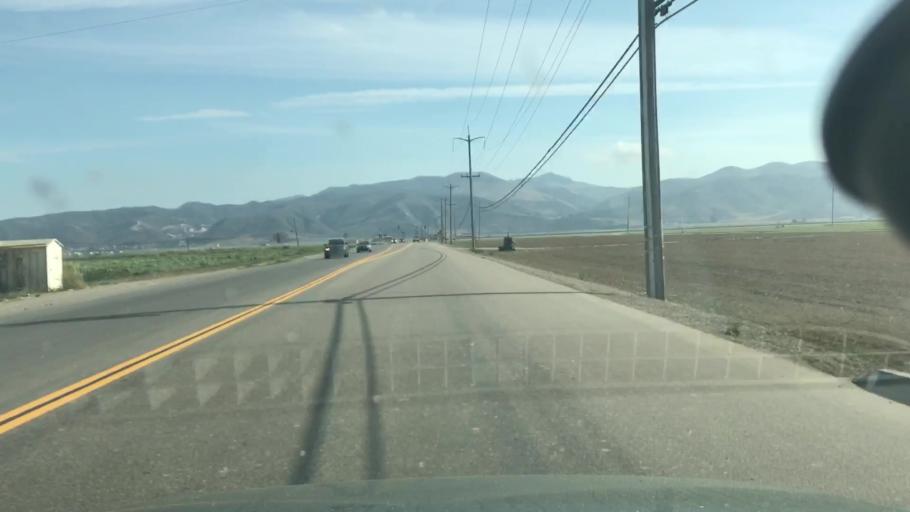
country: US
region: California
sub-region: Santa Barbara County
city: Lompoc
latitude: 34.6654
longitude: -120.4928
